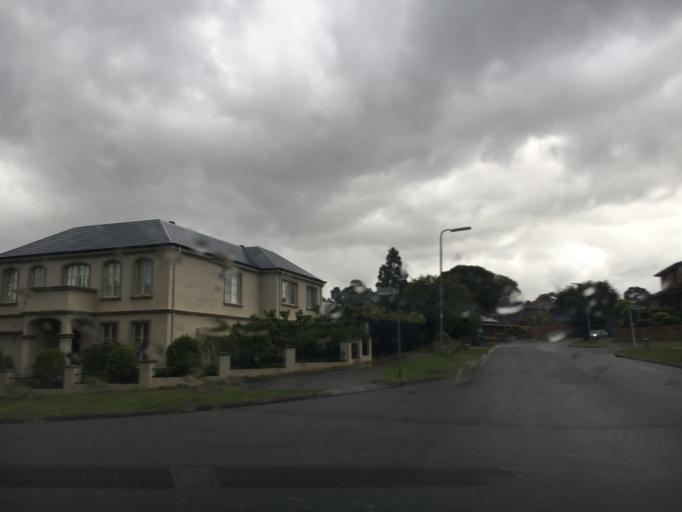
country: AU
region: Victoria
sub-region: Whitehorse
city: Vermont South
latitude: -37.8854
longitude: 145.1828
